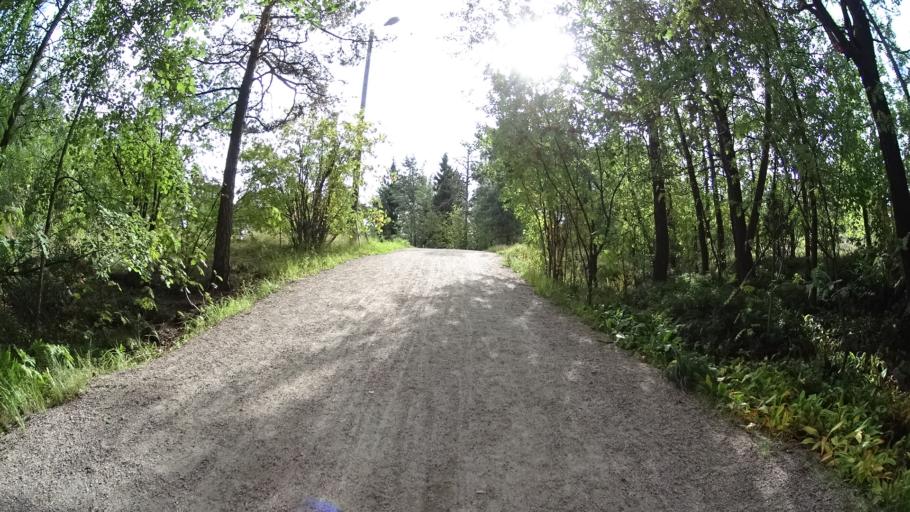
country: FI
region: Uusimaa
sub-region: Helsinki
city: Helsinki
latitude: 60.1960
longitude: 24.9090
